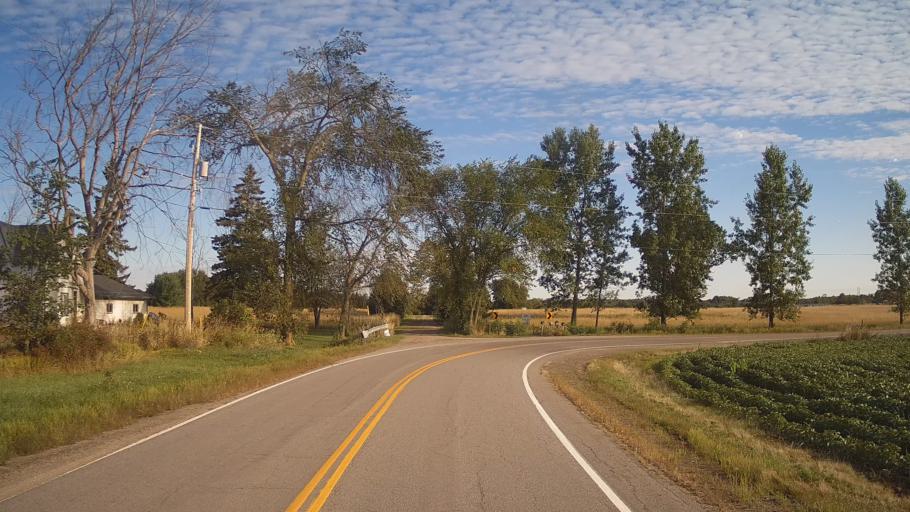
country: CA
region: Ontario
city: Gananoque
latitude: 44.3990
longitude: -76.1100
